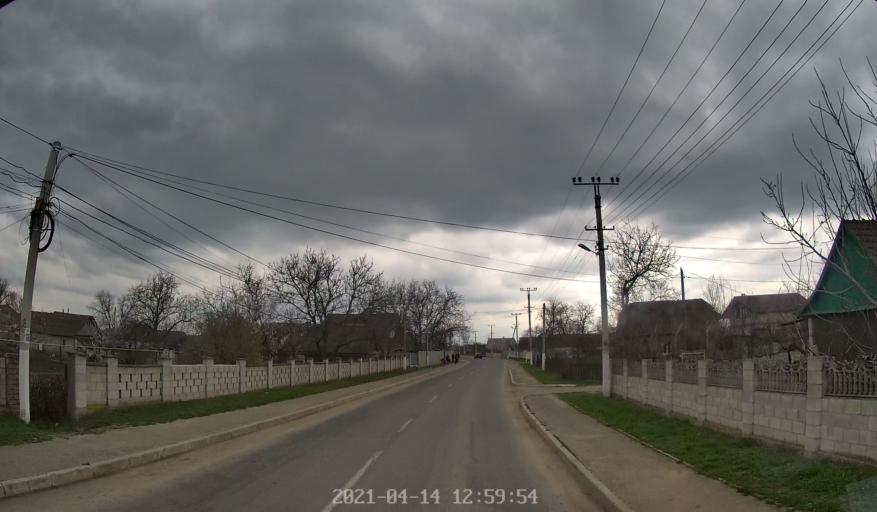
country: MD
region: Chisinau
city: Vadul lui Voda
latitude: 47.1422
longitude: 29.1236
